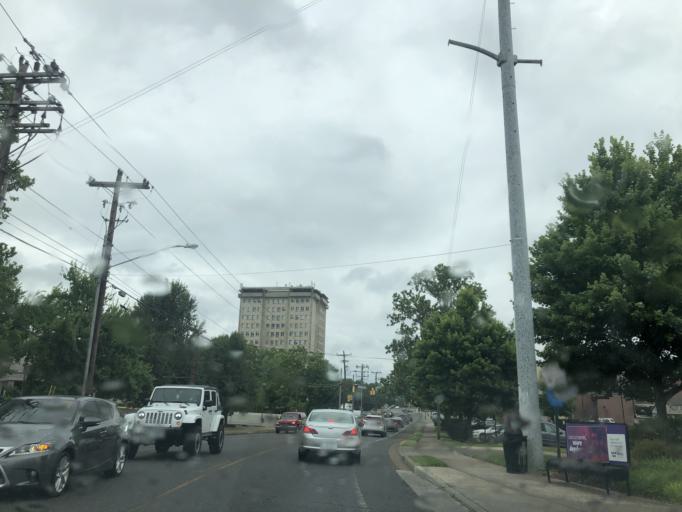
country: US
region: Tennessee
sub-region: Davidson County
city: Belle Meade
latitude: 36.1040
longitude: -86.8196
